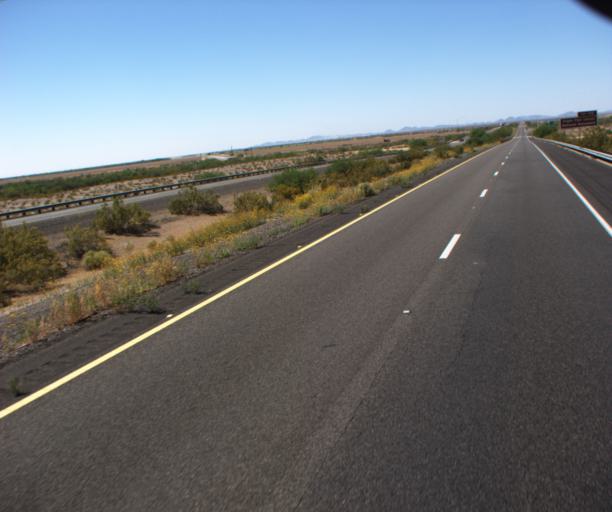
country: US
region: Arizona
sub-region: Maricopa County
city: Gila Bend
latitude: 32.9377
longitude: -112.7247
